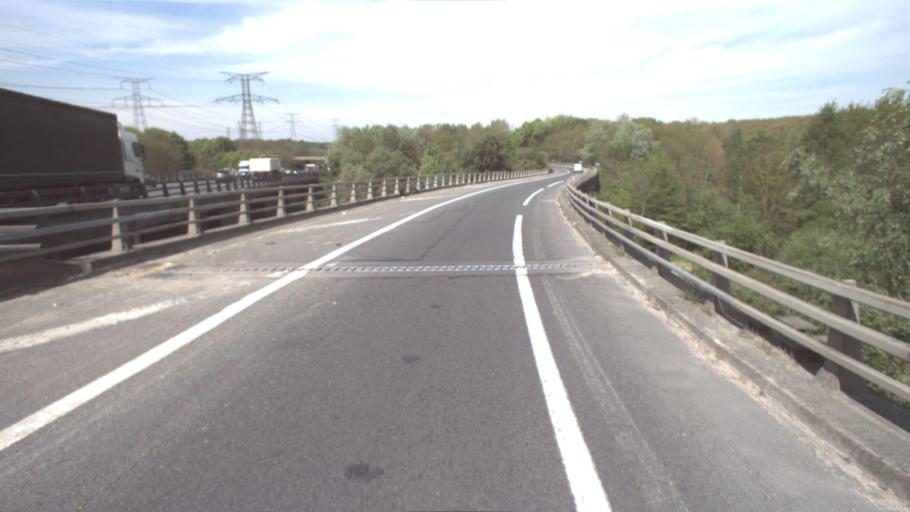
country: FR
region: Ile-de-France
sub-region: Departement de Seine-et-Marne
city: Saint-Thibault-des-Vignes
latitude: 48.8773
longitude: 2.6688
